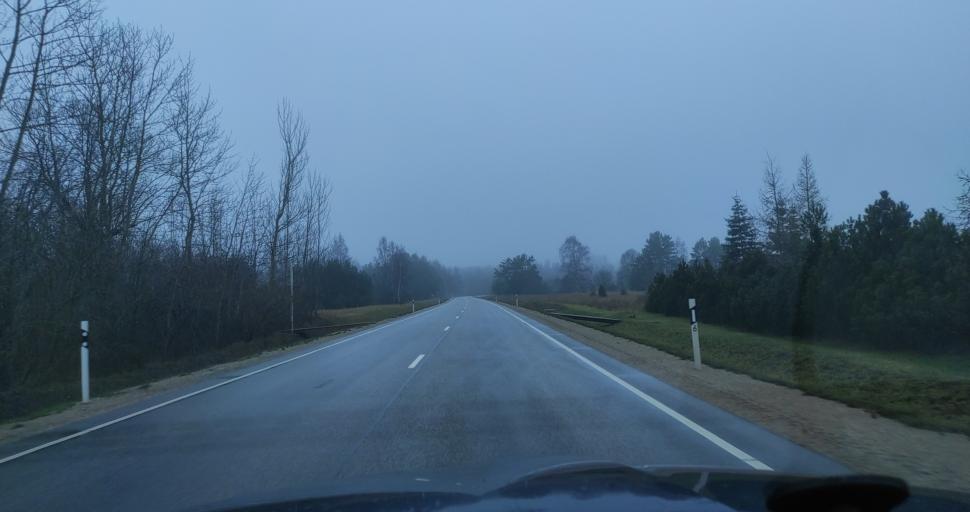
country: LV
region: Pavilostas
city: Pavilosta
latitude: 56.9267
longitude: 21.2675
